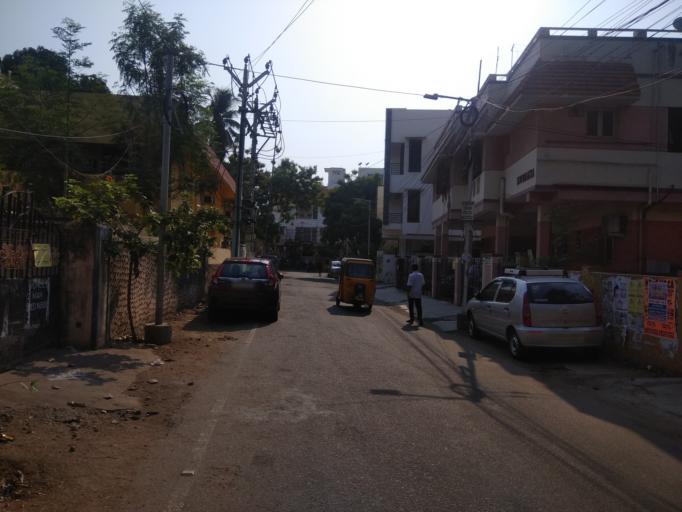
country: IN
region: Tamil Nadu
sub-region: Chennai
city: Gandhi Nagar
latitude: 13.0337
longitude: 80.2337
